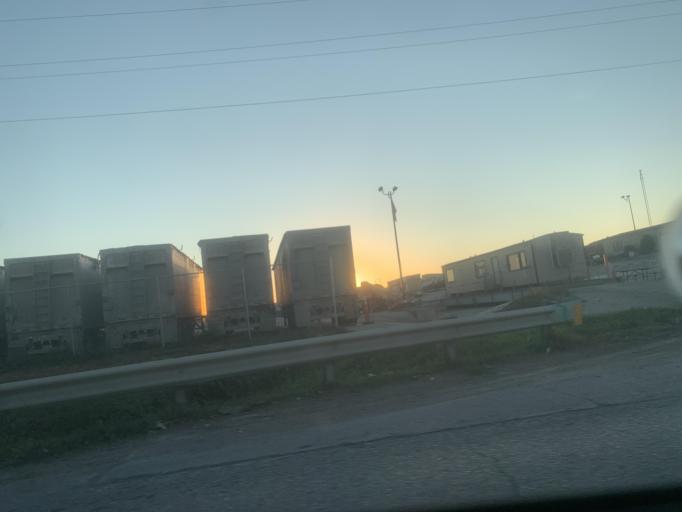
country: US
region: Nebraska
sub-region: Sarpy County
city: La Vista
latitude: 41.1949
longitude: -96.0073
